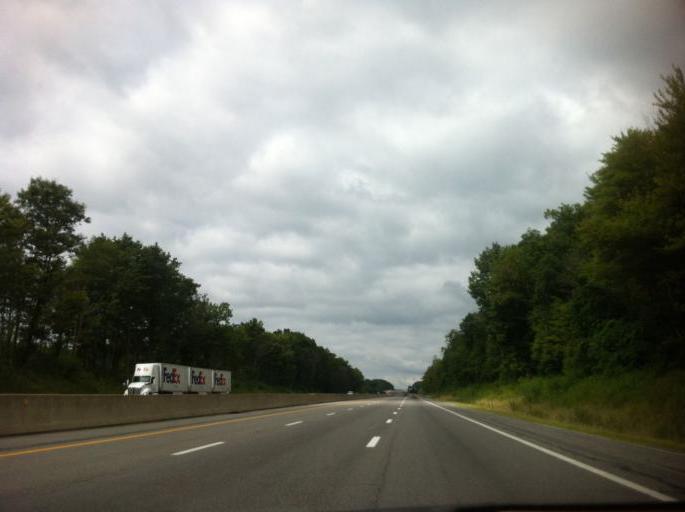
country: US
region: Ohio
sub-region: Portage County
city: Garrettsville
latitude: 41.2438
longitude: -81.1031
